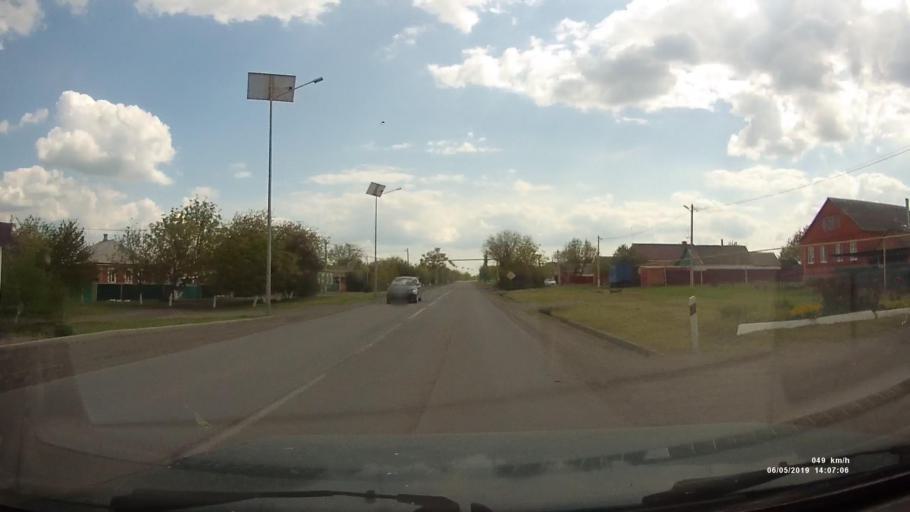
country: RU
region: Rostov
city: Shakhty
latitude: 47.6837
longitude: 40.3030
